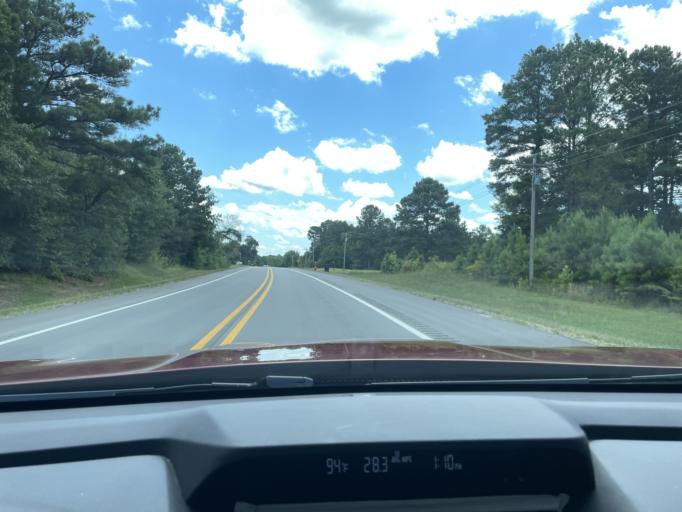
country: US
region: Arkansas
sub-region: Drew County
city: Monticello
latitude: 33.7138
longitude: -91.8107
